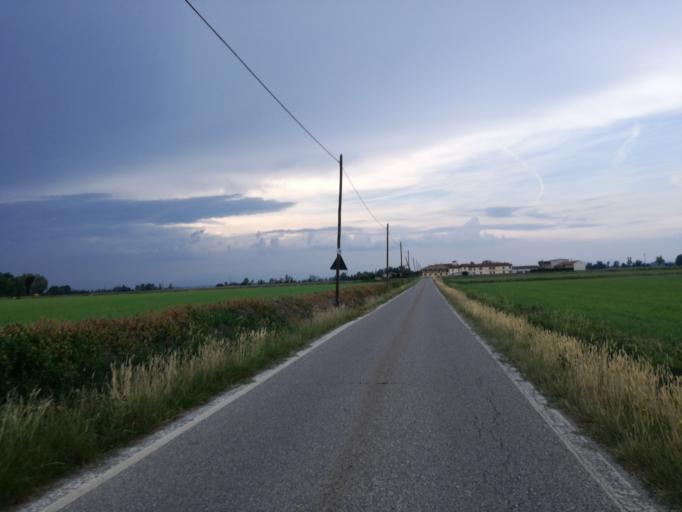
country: IT
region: Piedmont
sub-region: Provincia di Novara
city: Torrion Quartara
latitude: 45.3813
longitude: 8.6163
